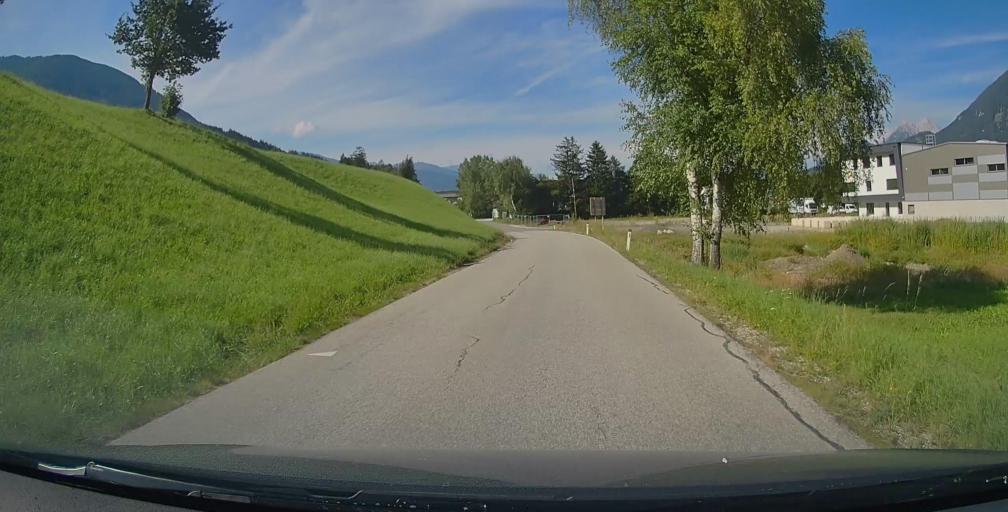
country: AT
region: Tyrol
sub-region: Politischer Bezirk Schwaz
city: Stans
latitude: 47.3573
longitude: 11.7317
